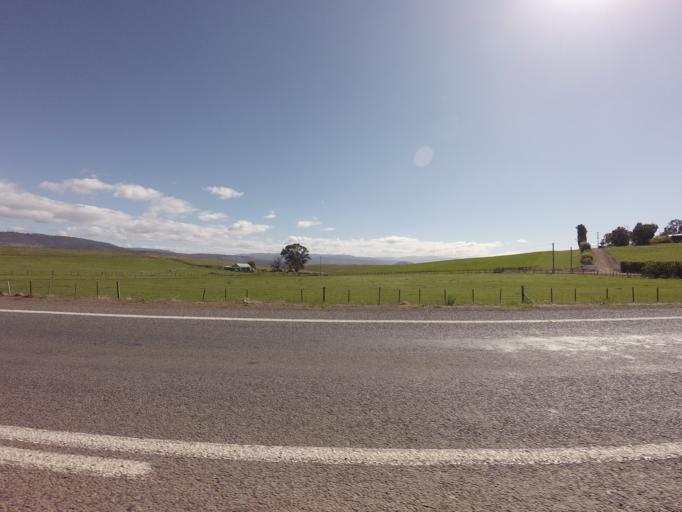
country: AU
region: Tasmania
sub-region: Derwent Valley
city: New Norfolk
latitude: -42.7020
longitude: 146.9419
